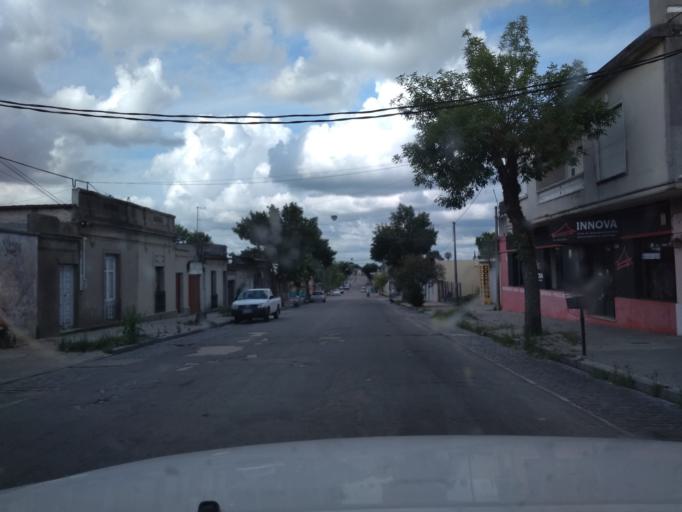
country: UY
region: Florida
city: Florida
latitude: -34.0925
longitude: -56.2178
